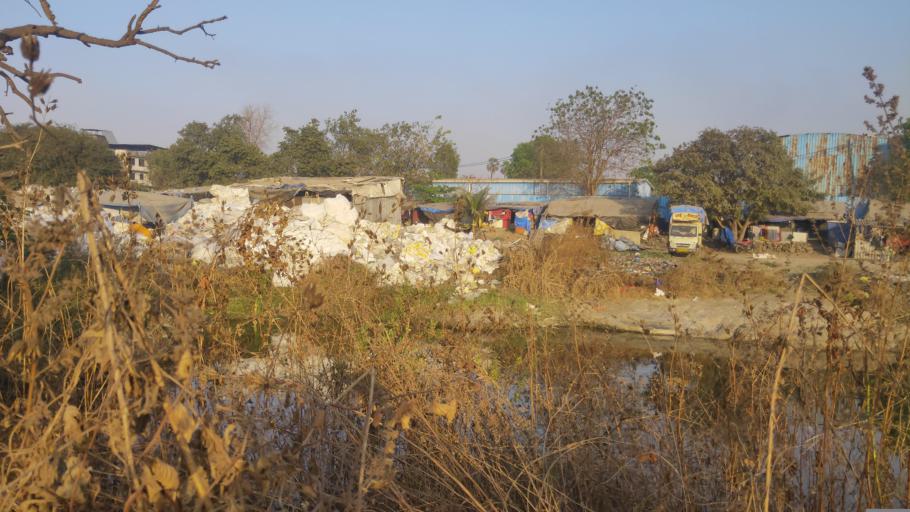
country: IN
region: Maharashtra
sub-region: Thane
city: Bhiwandi
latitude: 19.2491
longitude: 73.0288
